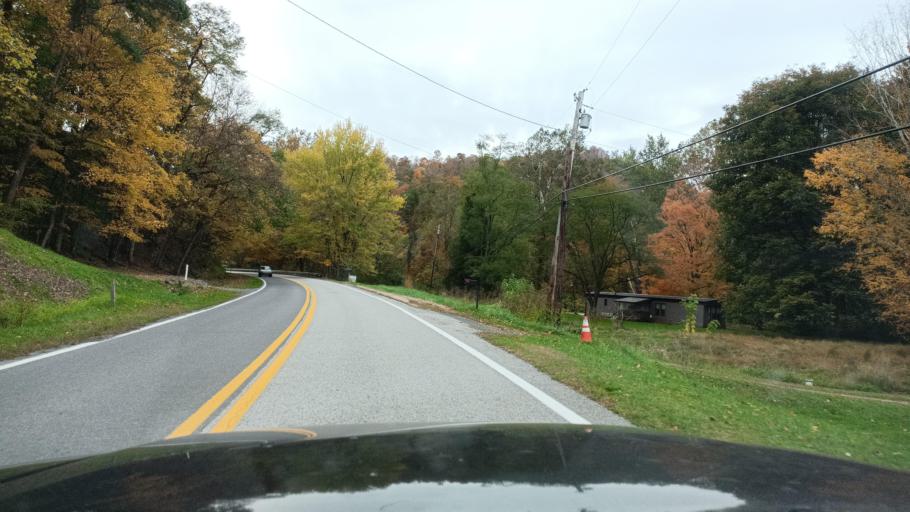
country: US
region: West Virginia
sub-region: Preston County
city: Kingwood
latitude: 39.3198
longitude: -79.6855
